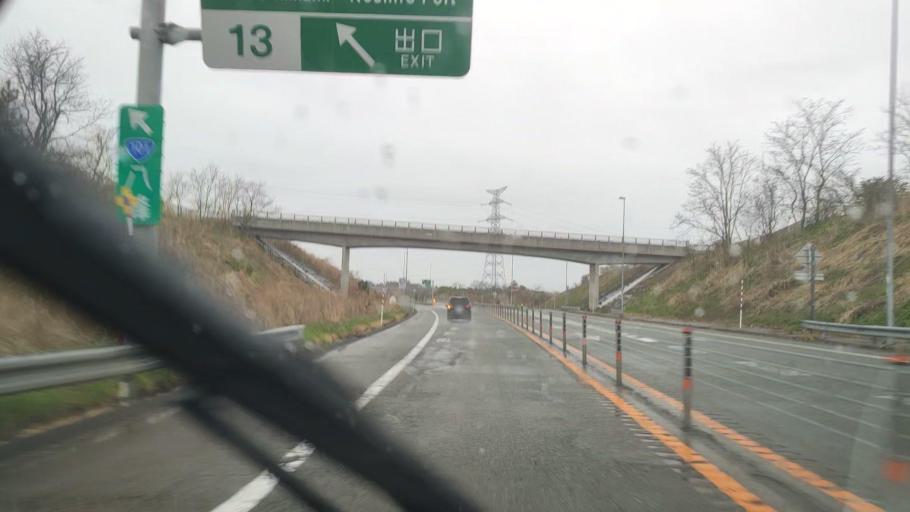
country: JP
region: Akita
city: Noshiromachi
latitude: 40.1565
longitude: 140.0251
